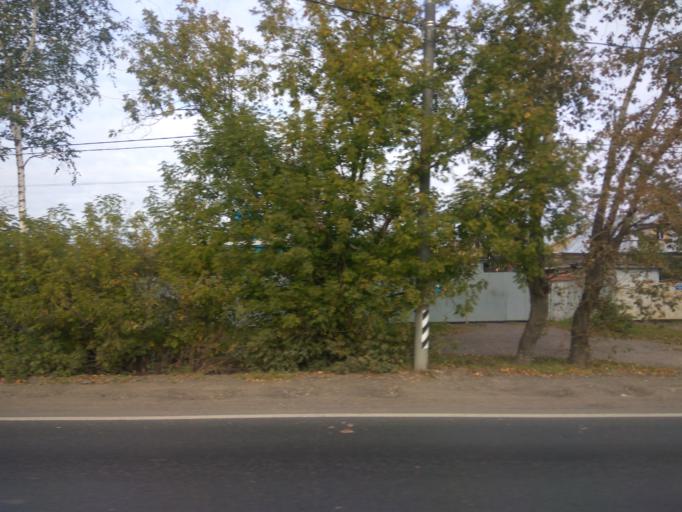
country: RU
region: Moskovskaya
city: Balashikha
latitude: 55.8419
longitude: 37.9515
